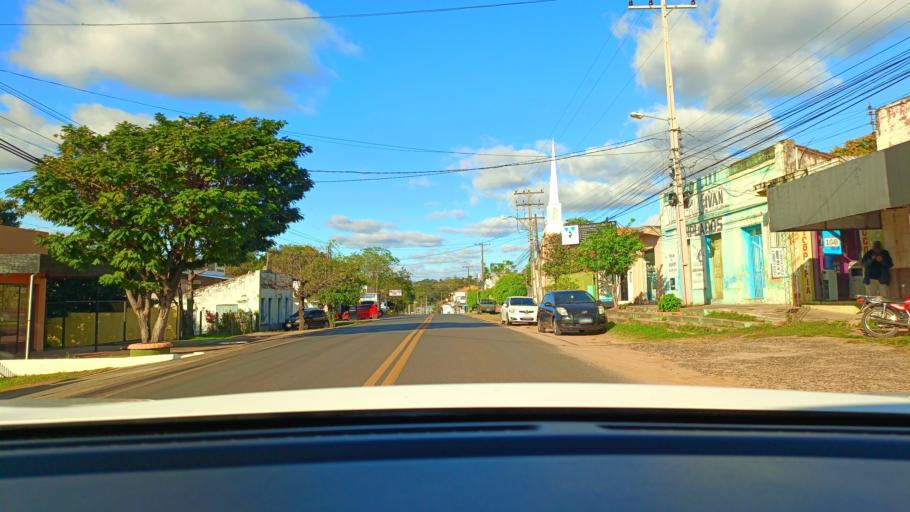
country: PY
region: San Pedro
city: Guayaybi
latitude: -24.6634
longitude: -56.4388
